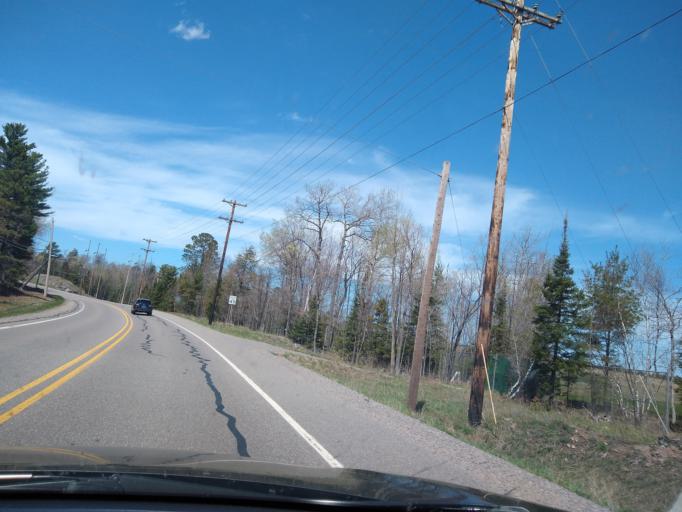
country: US
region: Michigan
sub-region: Marquette County
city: Trowbridge Park
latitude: 46.5767
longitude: -87.4227
